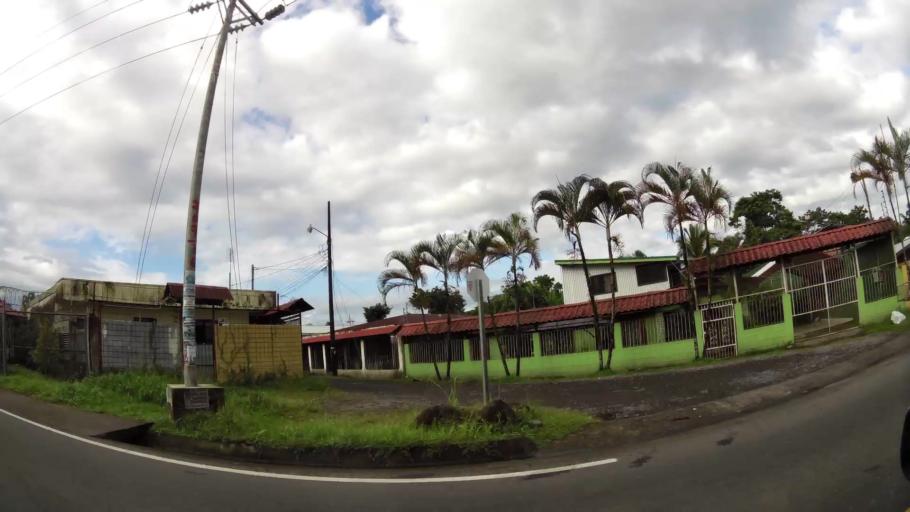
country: CR
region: Limon
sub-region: Canton de Pococi
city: Guapiles
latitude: 10.2130
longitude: -83.7810
